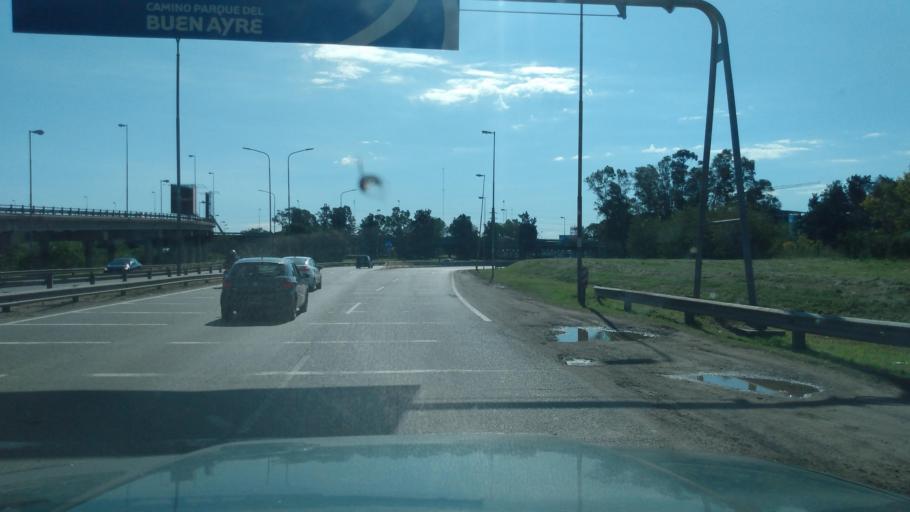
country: AR
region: Buenos Aires
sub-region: Partido de Tigre
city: Tigre
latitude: -34.4899
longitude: -58.5962
